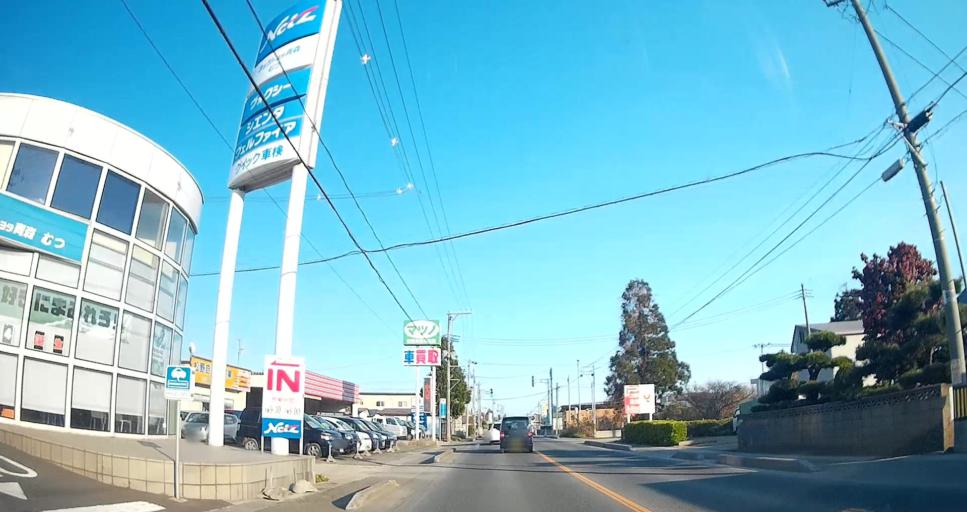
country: JP
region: Aomori
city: Mutsu
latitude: 41.2776
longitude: 141.2118
